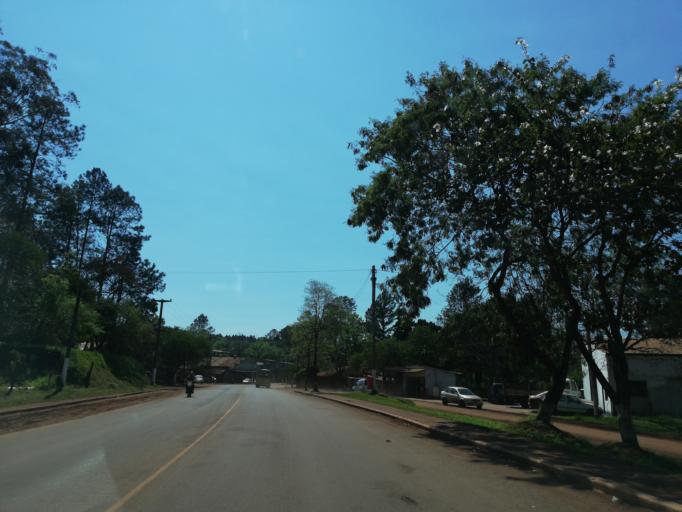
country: AR
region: Misiones
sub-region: Departamento de Eldorado
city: Eldorado
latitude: -26.4071
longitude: -54.6514
